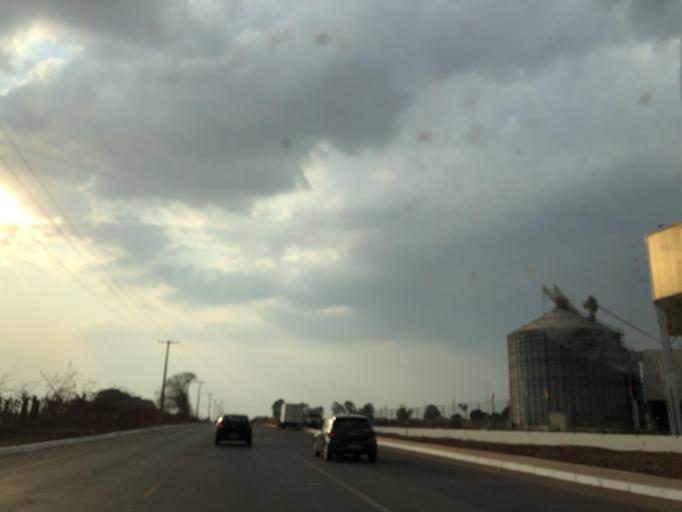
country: BR
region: Federal District
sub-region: Brasilia
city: Brasilia
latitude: -15.9305
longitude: -48.0468
